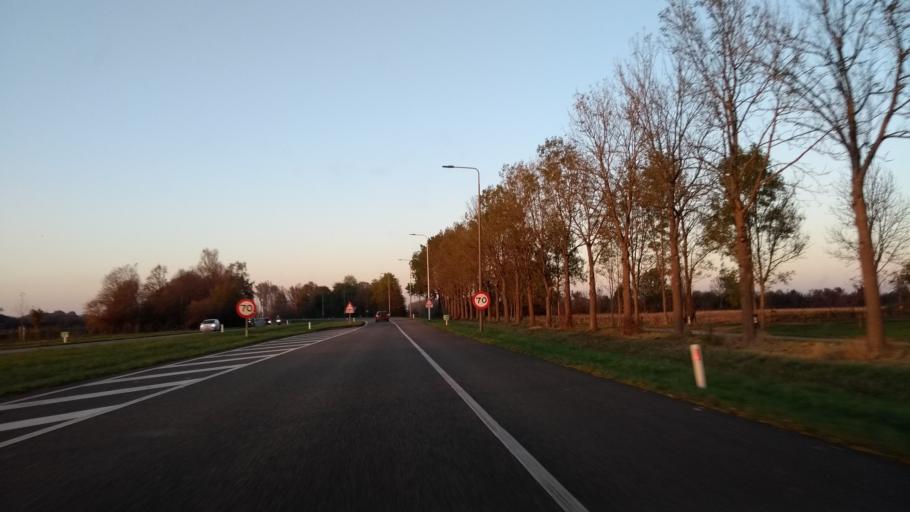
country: NL
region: Gelderland
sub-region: Gemeente Brummen
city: Brummen
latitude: 52.1046
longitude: 6.1684
